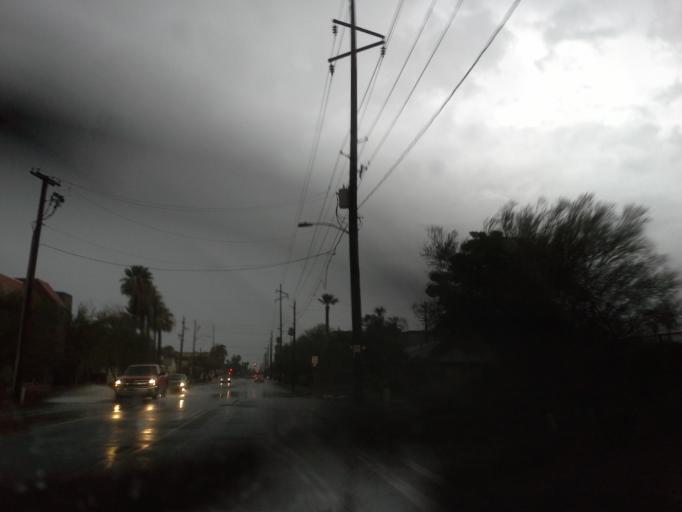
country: US
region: Arizona
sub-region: Maricopa County
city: Phoenix
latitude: 33.4766
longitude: -112.0726
